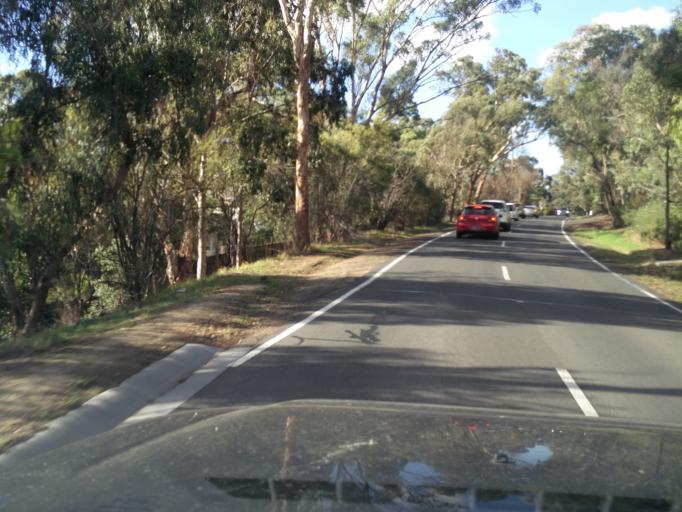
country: AU
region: Victoria
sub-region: Nillumbik
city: Eltham
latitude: -37.7259
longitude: 145.1521
